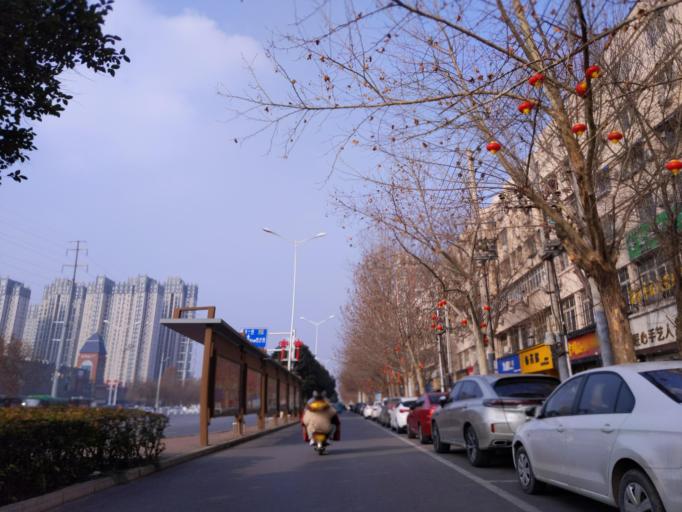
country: CN
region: Henan Sheng
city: Puyang
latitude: 35.7834
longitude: 115.0210
